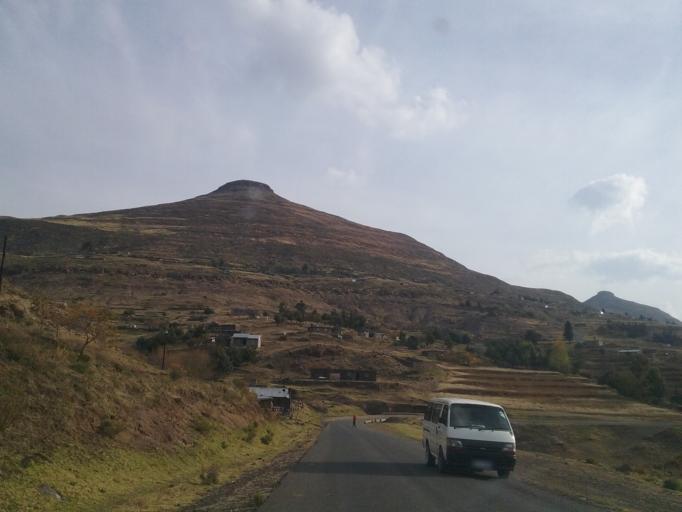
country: LS
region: Quthing
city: Quthing
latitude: -30.1935
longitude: 28.1222
